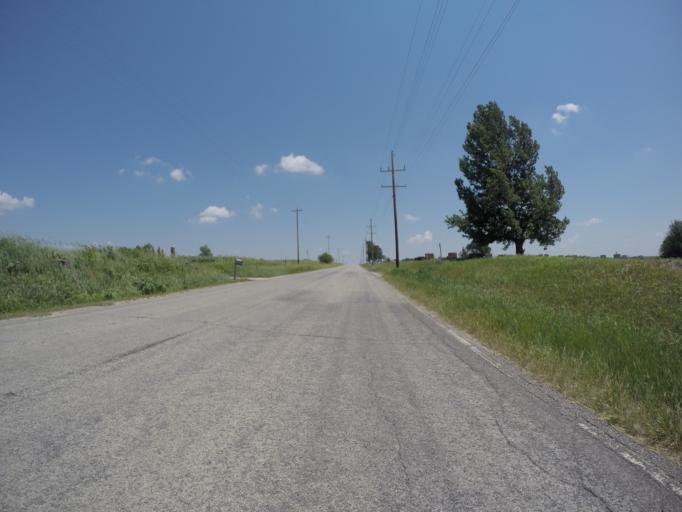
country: US
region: Kansas
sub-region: Doniphan County
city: Troy
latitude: 39.7690
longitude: -95.1050
